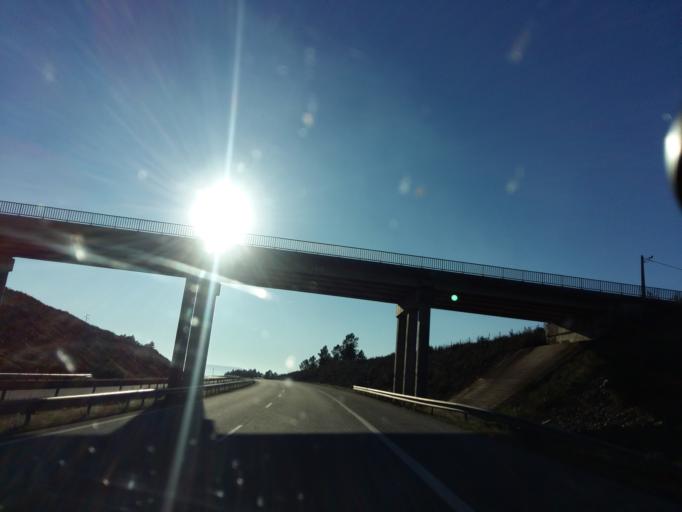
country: PT
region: Castelo Branco
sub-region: Castelo Branco
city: Castelo Branco
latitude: 39.7534
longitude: -7.6245
